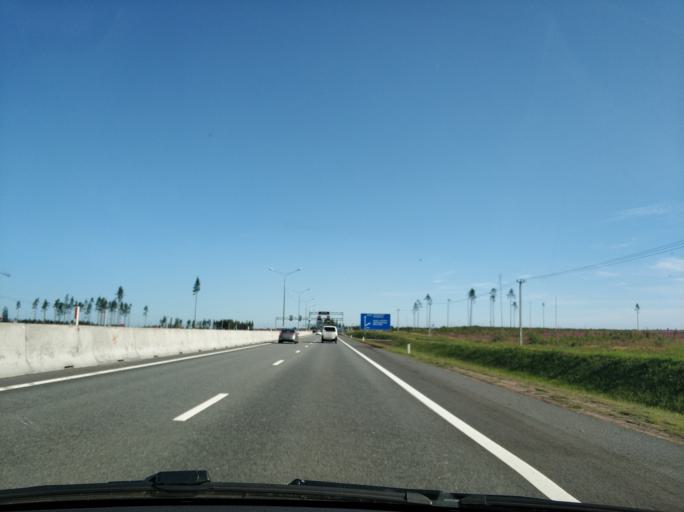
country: RU
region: Leningrad
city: Sosnovo
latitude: 60.4959
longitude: 30.1958
